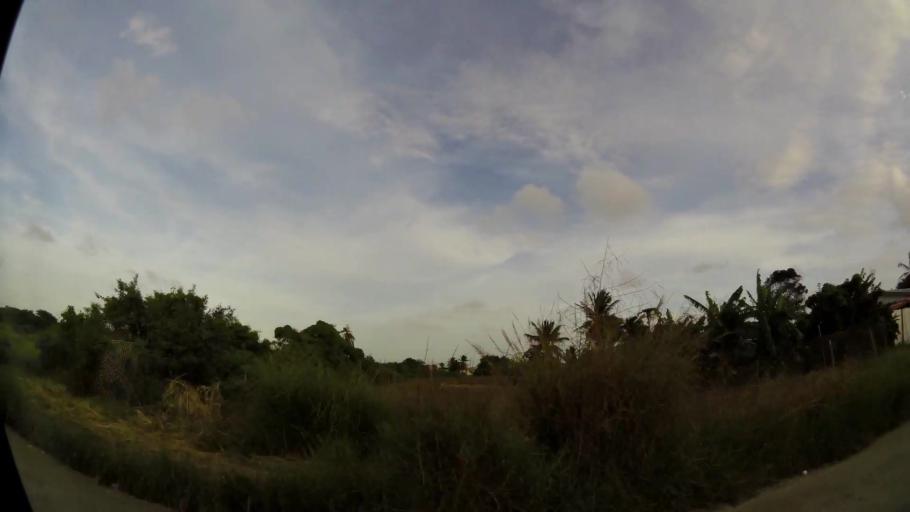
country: BB
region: Christ Church
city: Oistins
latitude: 13.0849
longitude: -59.4931
